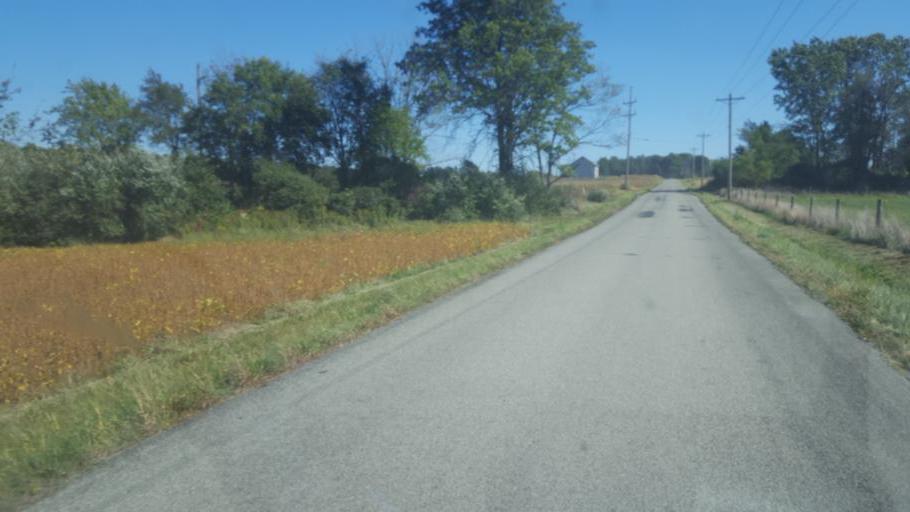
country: US
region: Ohio
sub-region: Huron County
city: Willard
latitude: 40.9490
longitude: -82.8408
